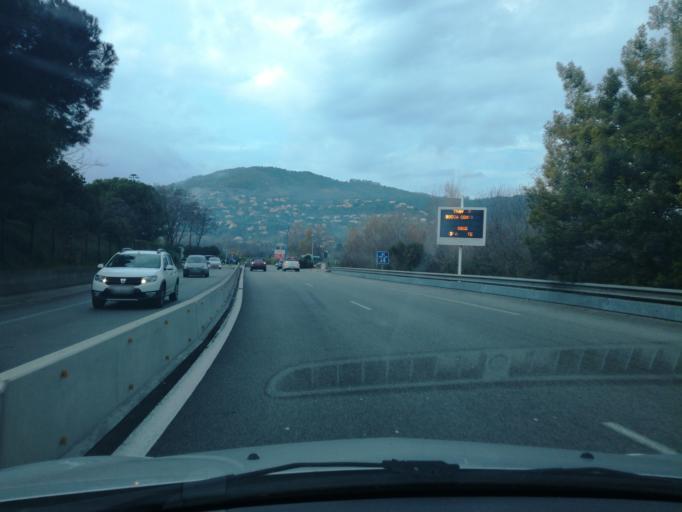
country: FR
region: Provence-Alpes-Cote d'Azur
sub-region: Departement des Alpes-Maritimes
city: Mandelieu-la-Napoule
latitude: 43.5611
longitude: 6.9524
